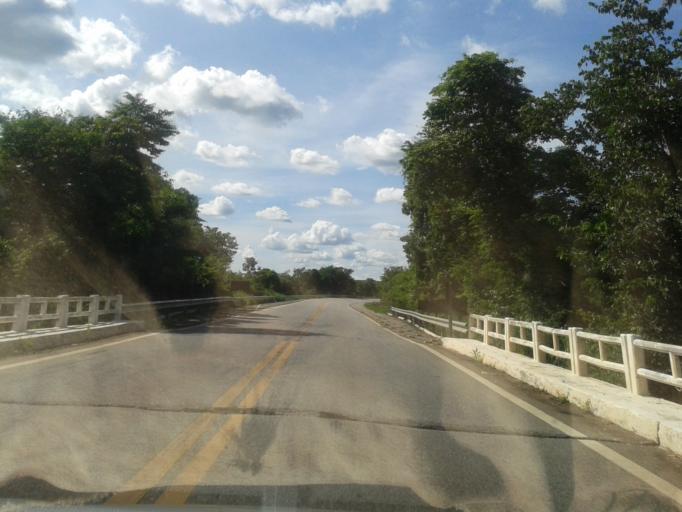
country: BR
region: Goias
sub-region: Mozarlandia
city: Mozarlandia
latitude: -15.1792
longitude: -50.5596
